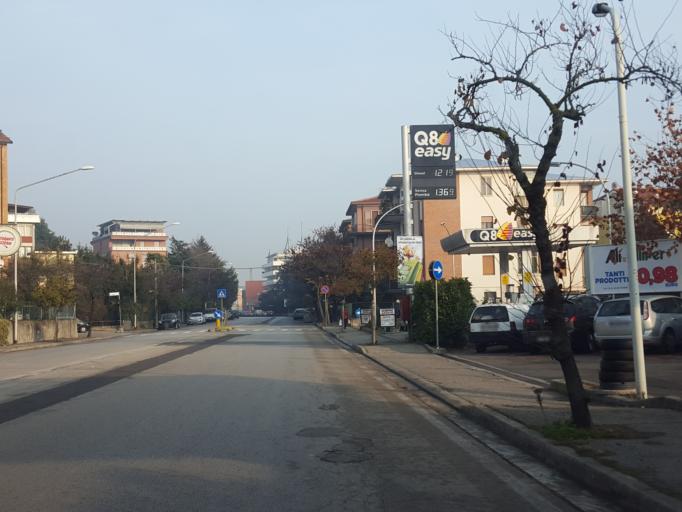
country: IT
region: Veneto
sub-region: Provincia di Vicenza
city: Vicenza
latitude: 45.5499
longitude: 11.5635
